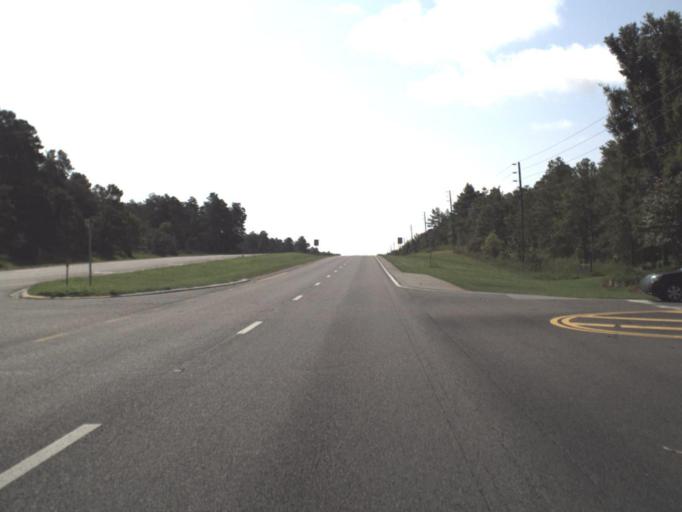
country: US
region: Florida
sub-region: Citrus County
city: Sugarmill Woods
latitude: 28.7117
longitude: -82.5334
